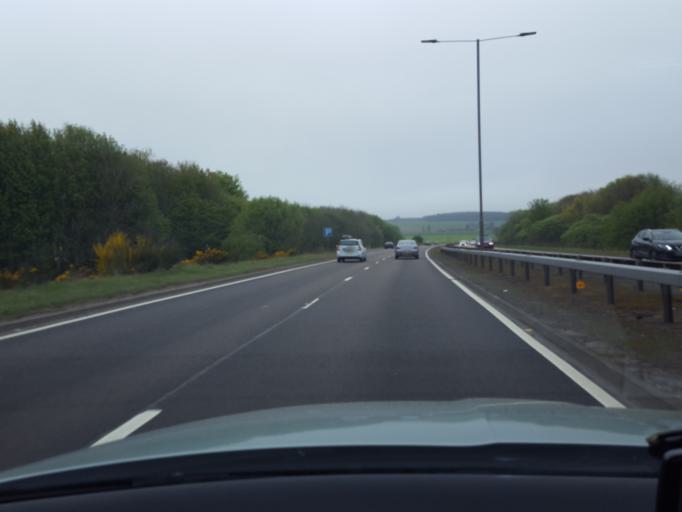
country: GB
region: Scotland
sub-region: Dundee City
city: Dundee
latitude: 56.5339
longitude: -2.9464
